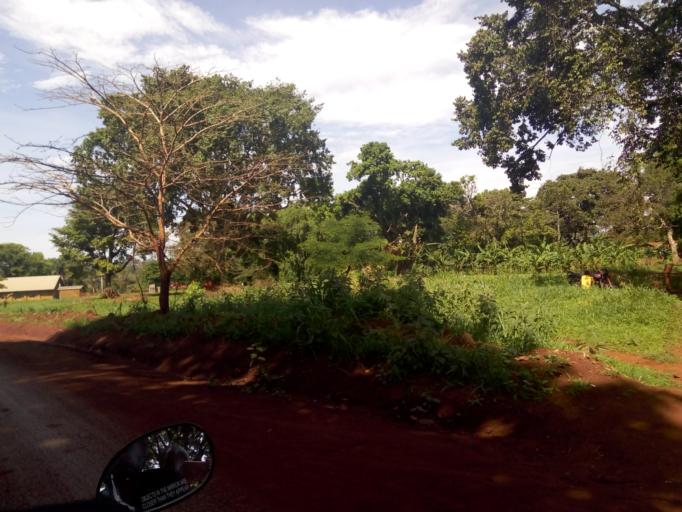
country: UG
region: Western Region
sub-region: Masindi District
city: Masindi
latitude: 1.6902
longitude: 31.7174
